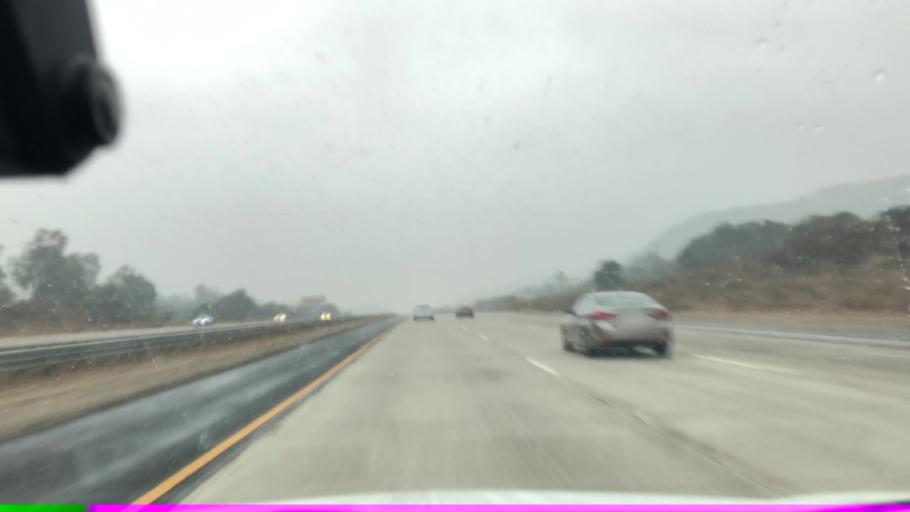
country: US
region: California
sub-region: San Diego County
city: Hidden Meadows
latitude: 33.1875
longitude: -117.1203
